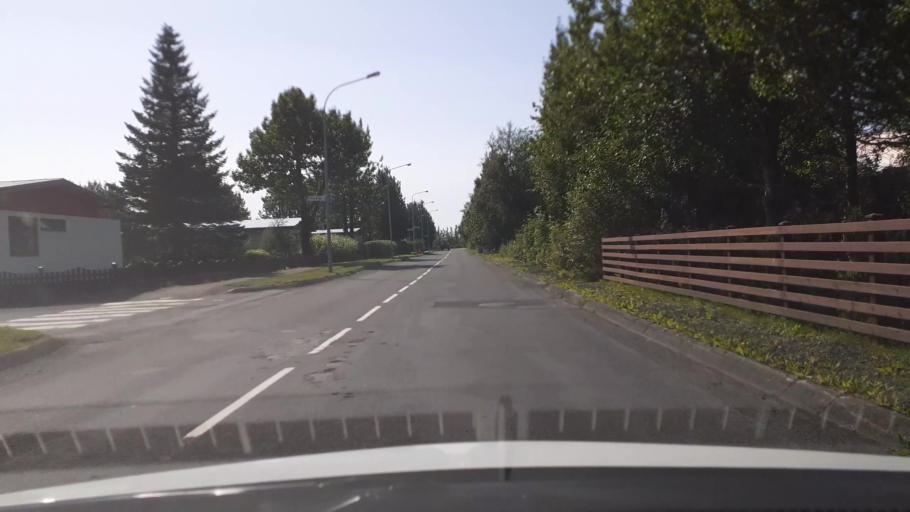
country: IS
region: South
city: Selfoss
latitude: 63.9313
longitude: -21.0089
